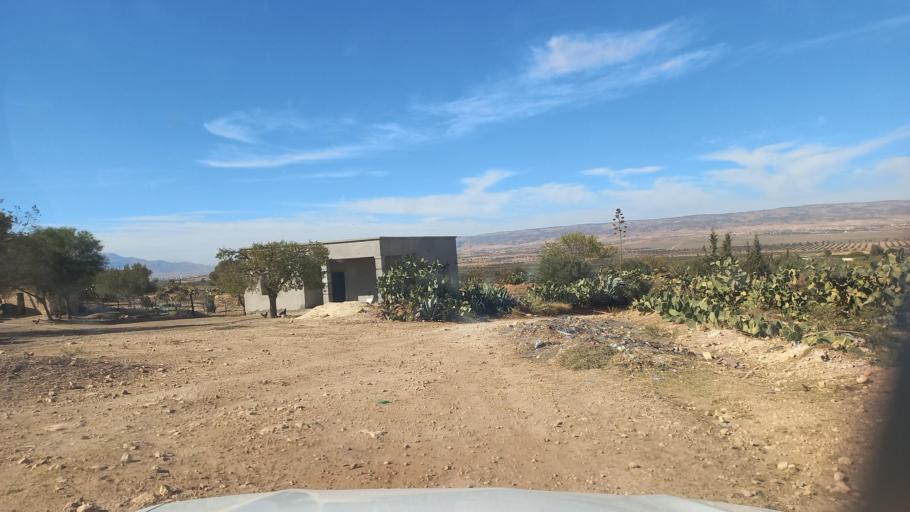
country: TN
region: Al Qasrayn
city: Kasserine
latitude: 35.2014
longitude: 8.9714
